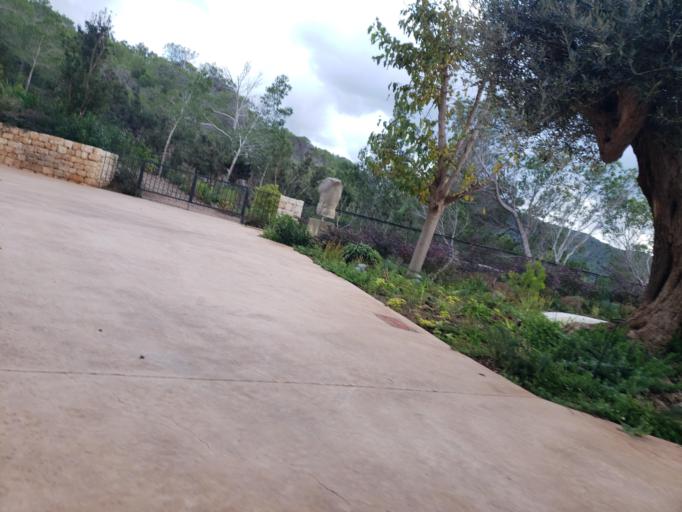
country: ES
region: Balearic Islands
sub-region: Illes Balears
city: Sant Joan de Labritja
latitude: 39.1104
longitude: 1.5074
